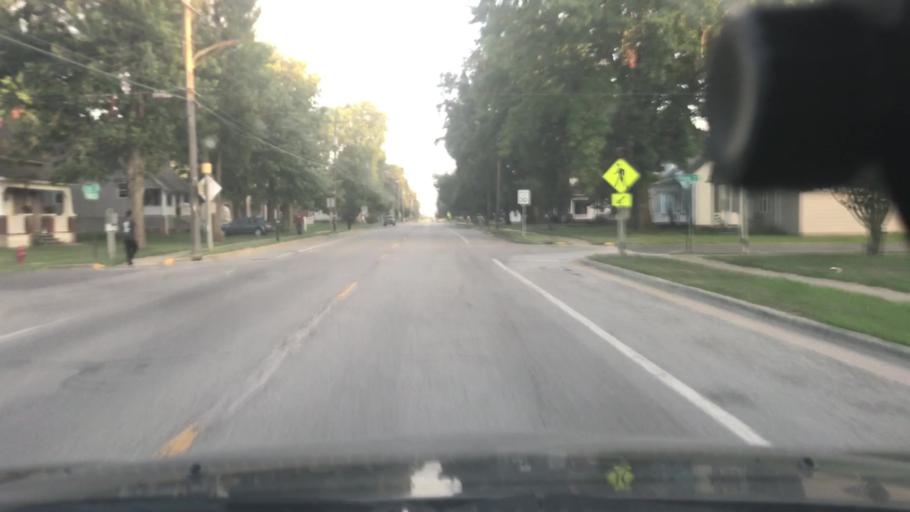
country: US
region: Illinois
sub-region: Washington County
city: Okawville
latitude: 38.4301
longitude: -89.5506
